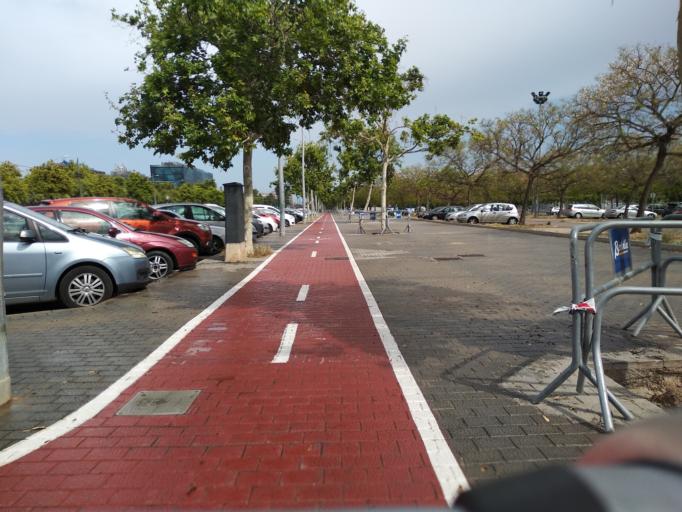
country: ES
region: Valencia
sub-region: Provincia de Valencia
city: Alboraya
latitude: 39.4775
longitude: -0.3381
